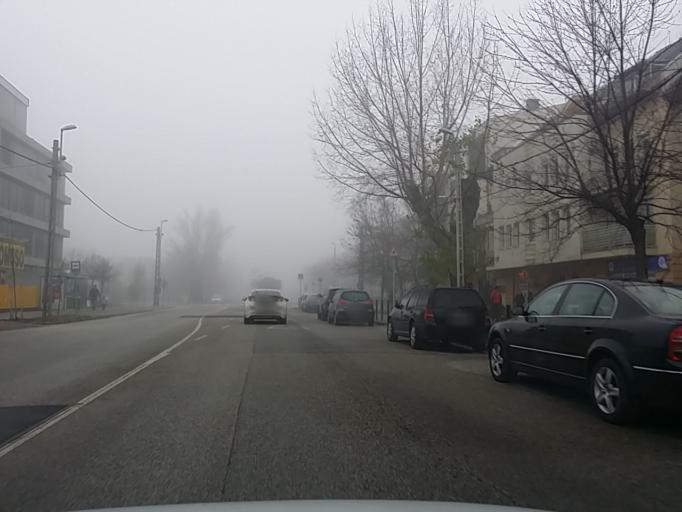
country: HU
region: Budapest
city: Budapest XIII. keruelet
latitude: 47.5391
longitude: 19.0767
